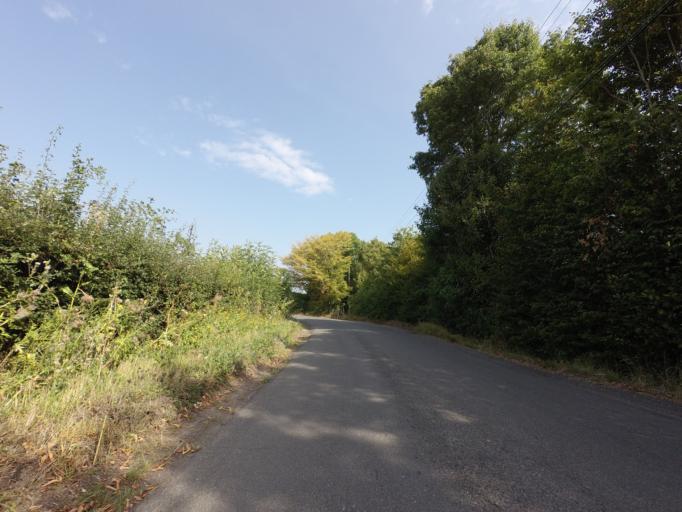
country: GB
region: England
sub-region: Kent
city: Staplehurst
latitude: 51.1263
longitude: 0.5833
